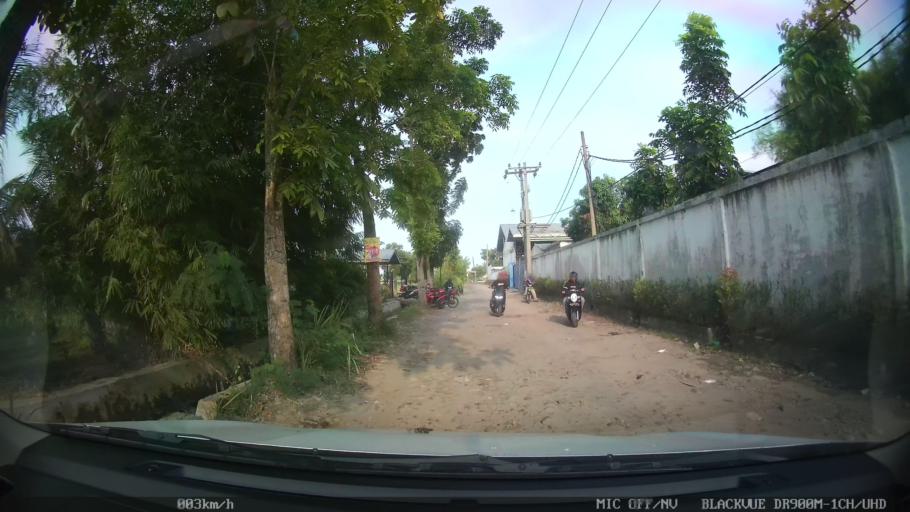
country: ID
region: North Sumatra
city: Binjai
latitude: 3.6174
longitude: 98.5334
